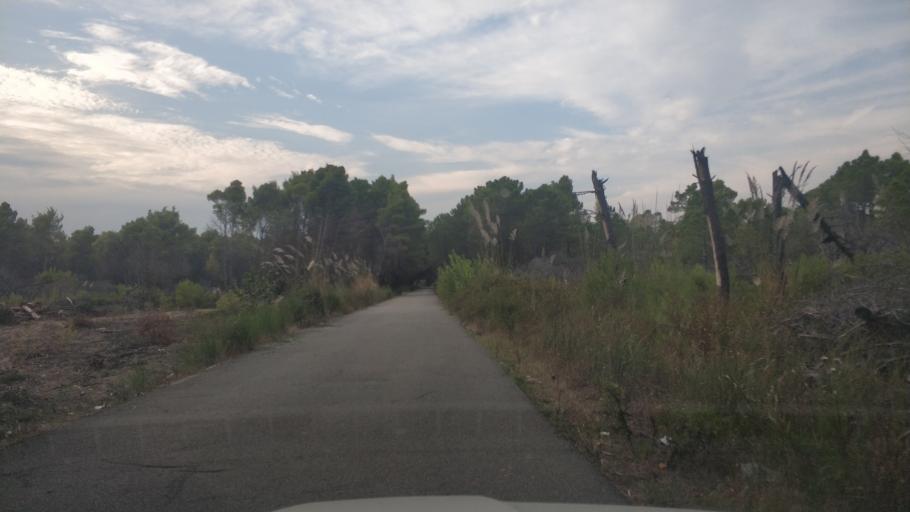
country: AL
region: Vlore
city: Vlore
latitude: 40.4938
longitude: 19.4348
